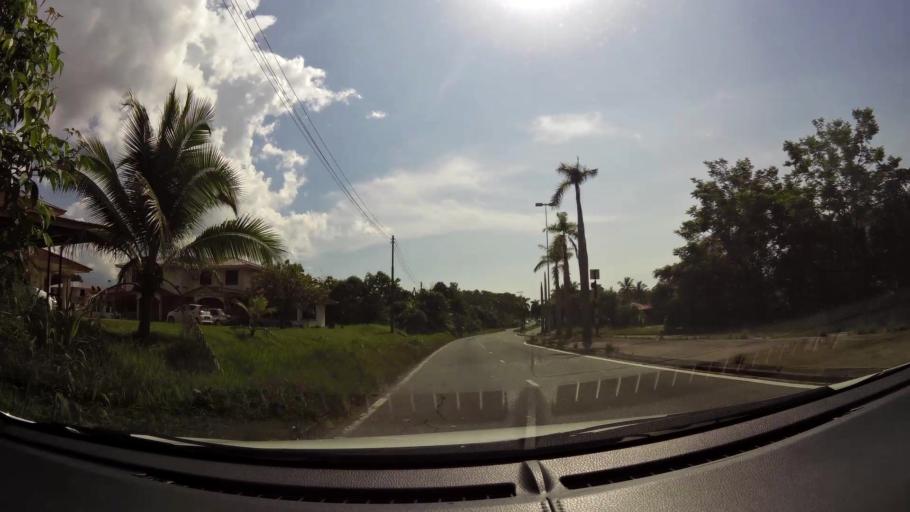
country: BN
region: Brunei and Muara
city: Bandar Seri Begawan
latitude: 4.9628
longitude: 114.9556
